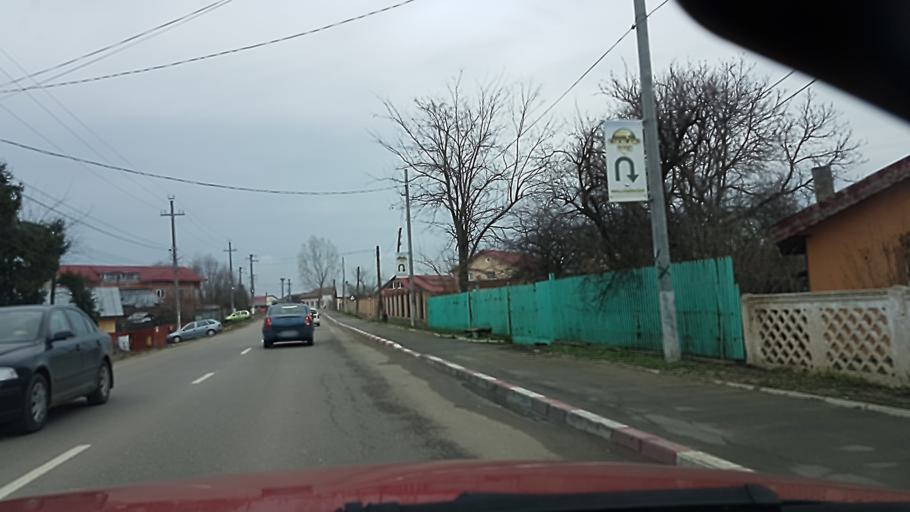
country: RO
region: Ilfov
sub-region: Comuna Balotesti
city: Balotesti
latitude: 44.6209
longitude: 26.1182
